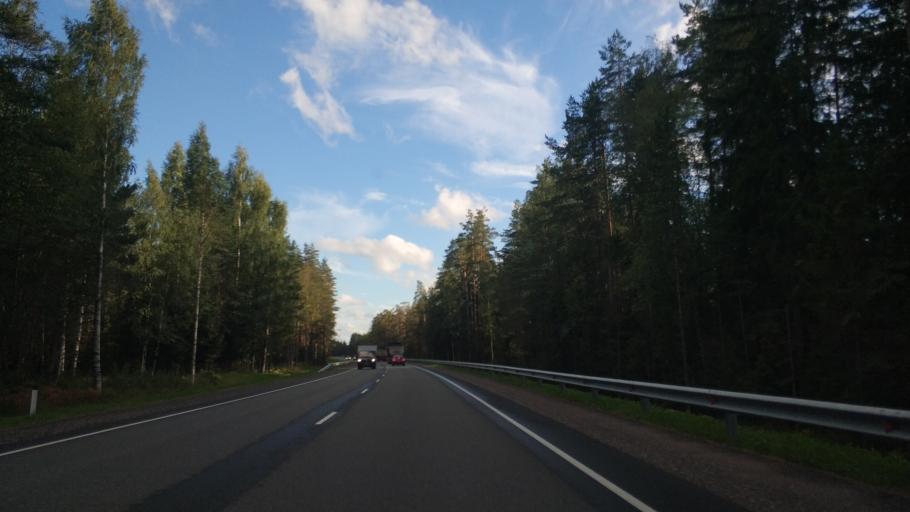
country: RU
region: Leningrad
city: Priozersk
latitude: 60.8925
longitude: 30.1596
